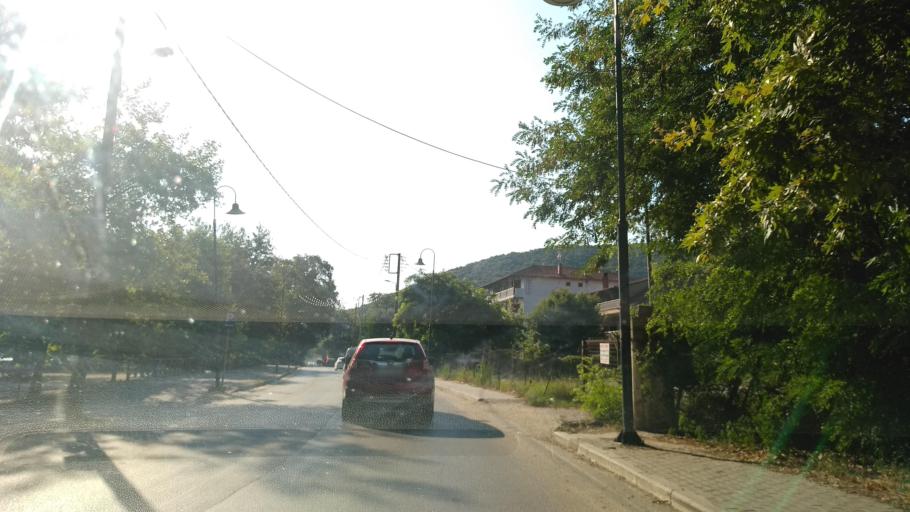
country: GR
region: Central Macedonia
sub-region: Nomos Thessalonikis
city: Stavros
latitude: 40.6641
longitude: 23.7028
